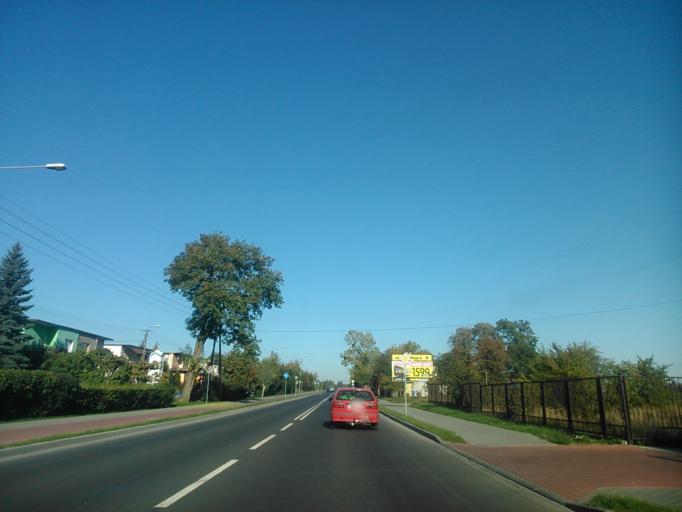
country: PL
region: Kujawsko-Pomorskie
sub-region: Powiat wabrzeski
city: Wabrzezno
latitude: 53.2734
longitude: 18.9683
